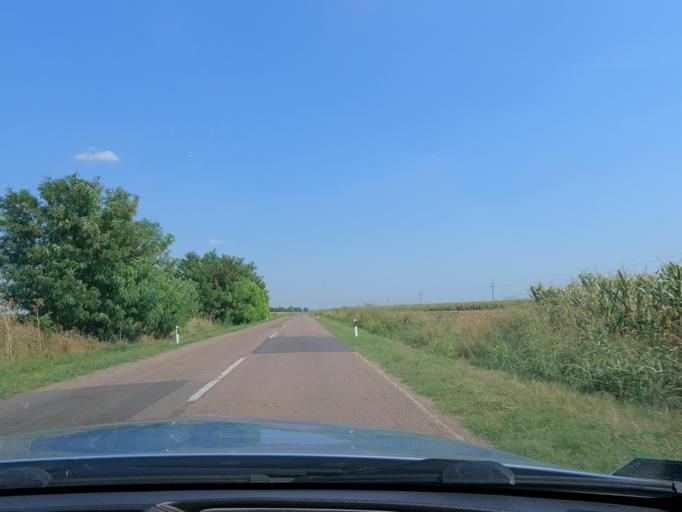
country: RS
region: Autonomna Pokrajina Vojvodina
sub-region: Severnobacki Okrug
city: Mali Igos
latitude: 45.7573
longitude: 19.7694
